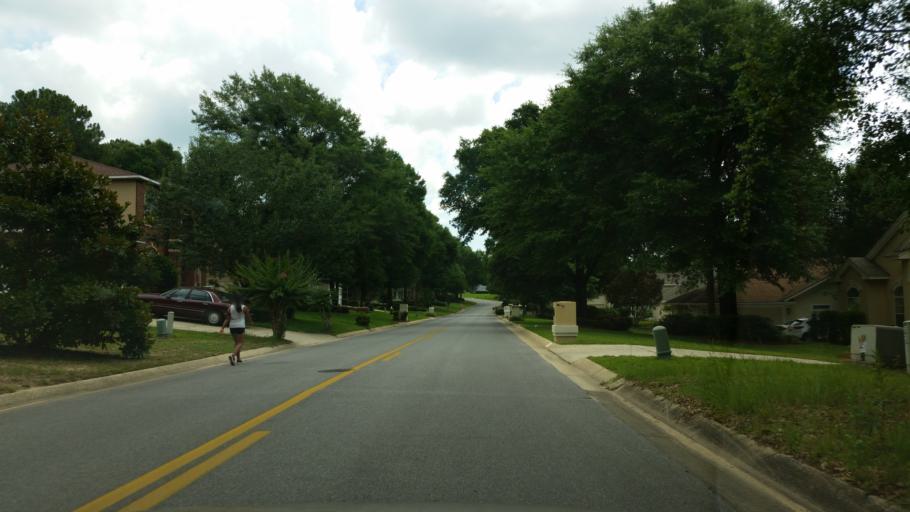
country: US
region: Florida
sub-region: Escambia County
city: Bellview
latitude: 30.4805
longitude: -87.2821
